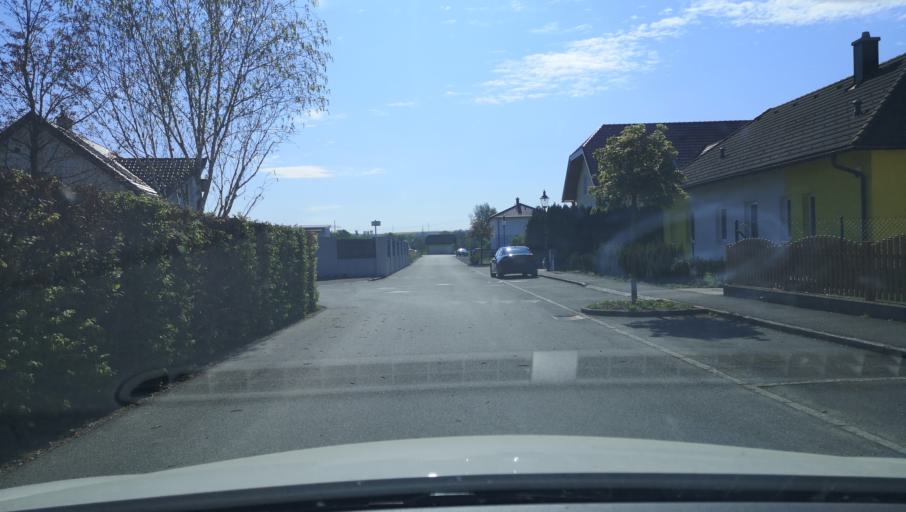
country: AT
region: Lower Austria
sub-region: Politischer Bezirk Melk
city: Petzenkirchen
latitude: 48.1405
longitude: 15.1504
